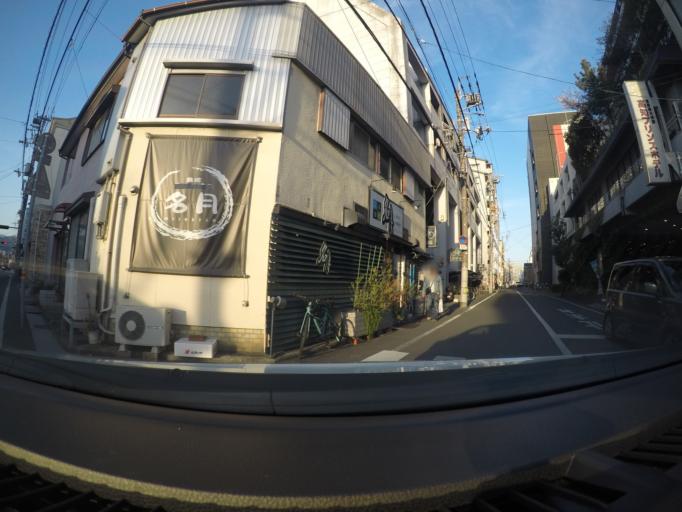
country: JP
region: Kochi
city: Kochi-shi
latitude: 33.5581
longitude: 133.5537
